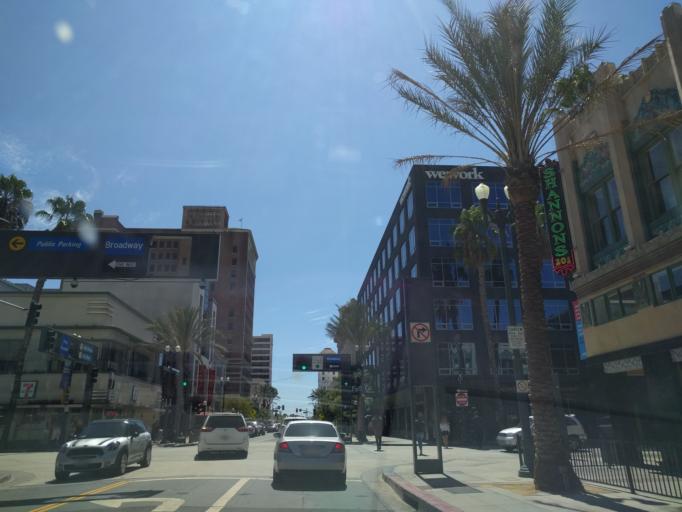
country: US
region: California
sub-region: Los Angeles County
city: Long Beach
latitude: 33.7696
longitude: -118.1927
